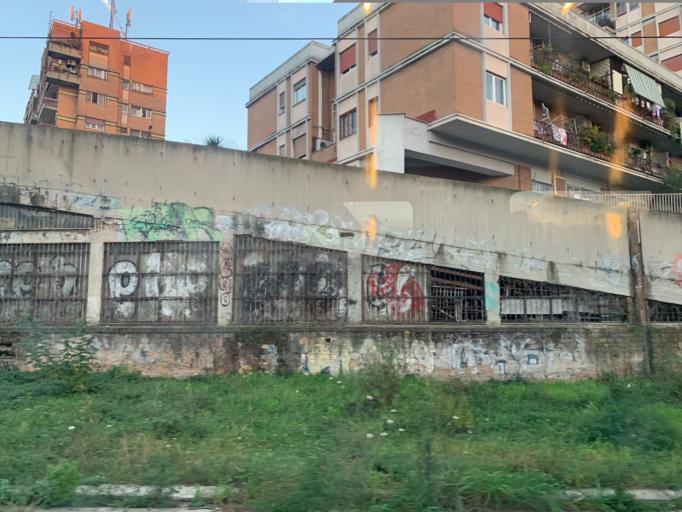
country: VA
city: Vatican City
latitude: 41.8693
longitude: 12.4607
